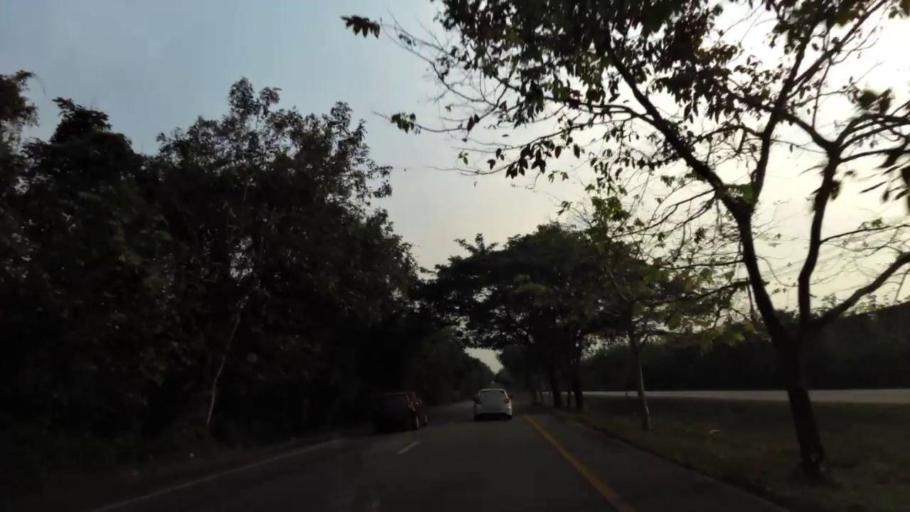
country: TH
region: Chanthaburi
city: Chanthaburi
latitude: 12.5360
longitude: 102.1576
